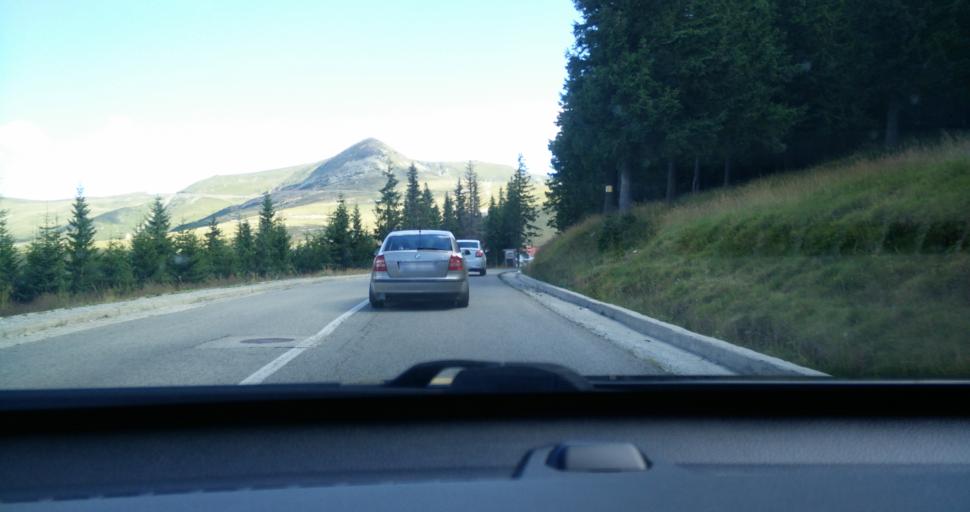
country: RO
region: Gorj
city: Novaci-Straini
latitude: 45.3006
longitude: 23.6811
